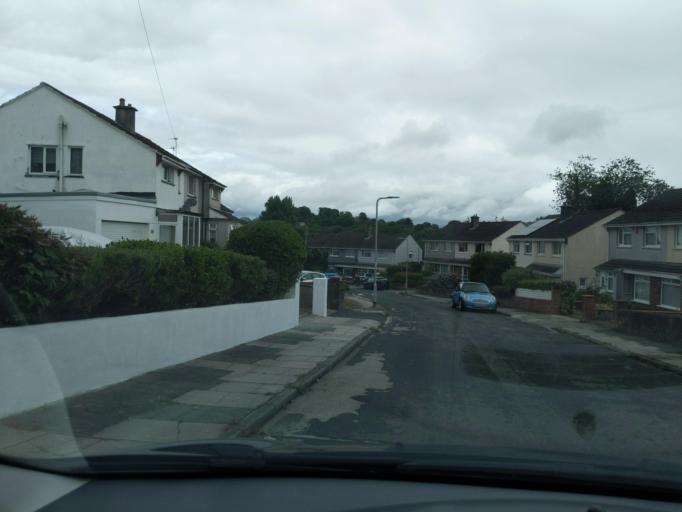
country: GB
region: England
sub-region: Plymouth
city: Plymouth
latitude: 50.3987
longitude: -4.1419
